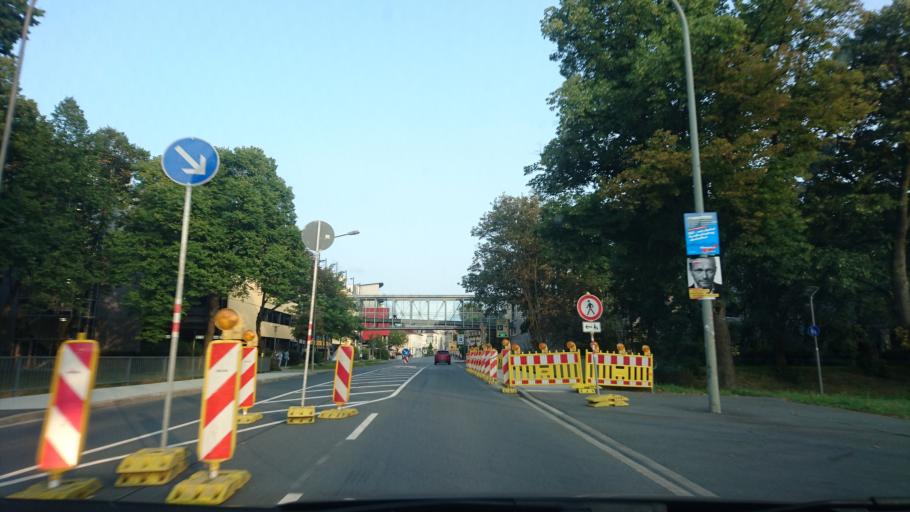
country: DE
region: Bavaria
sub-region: Upper Franconia
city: Bayreuth
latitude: 49.9472
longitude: 11.5682
